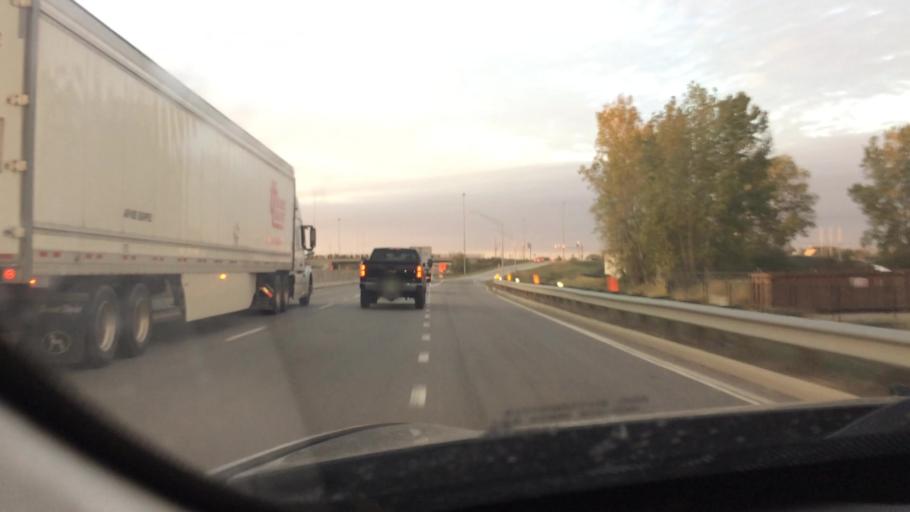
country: US
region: Ohio
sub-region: Hancock County
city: Findlay
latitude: 41.0454
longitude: -83.6730
